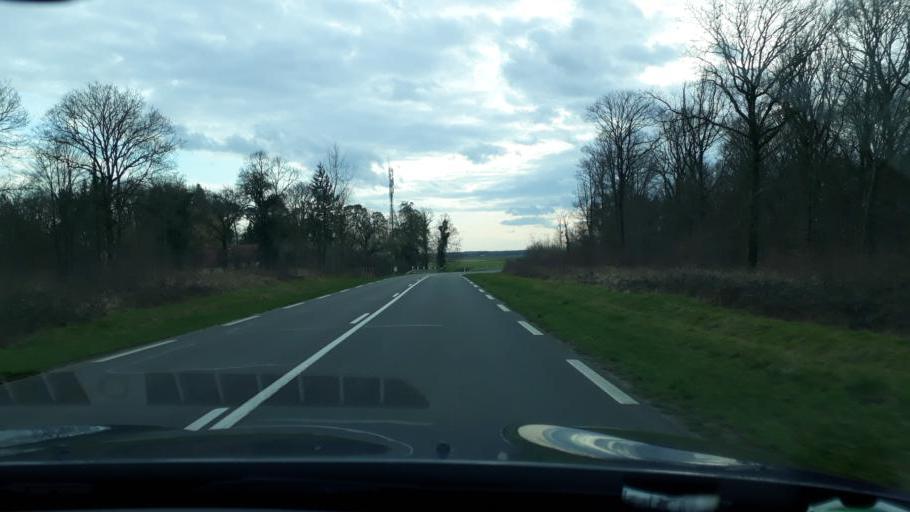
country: FR
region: Centre
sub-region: Departement du Loiret
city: Loury
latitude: 48.0207
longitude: 2.1143
